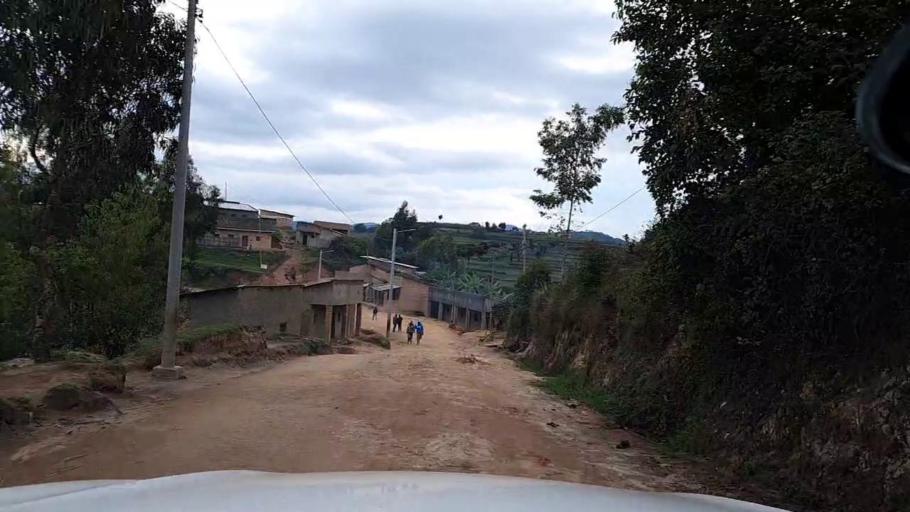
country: BI
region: Kayanza
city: Kayanza
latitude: -2.7979
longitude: 29.4956
